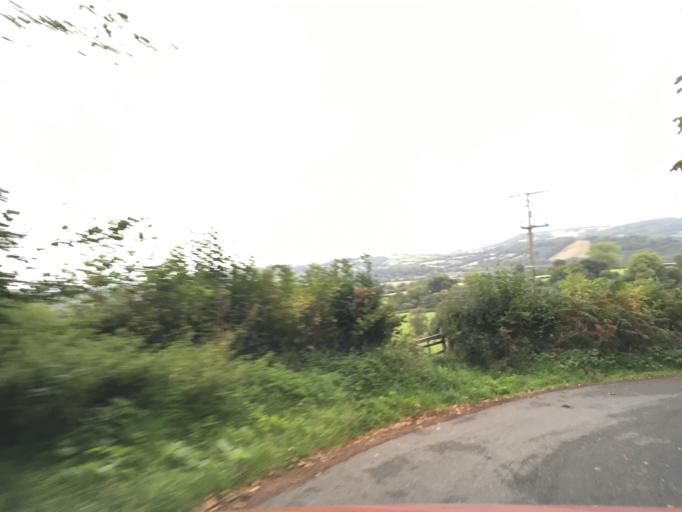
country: GB
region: Wales
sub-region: Monmouthshire
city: Llangybi
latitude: 51.6478
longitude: -2.9145
